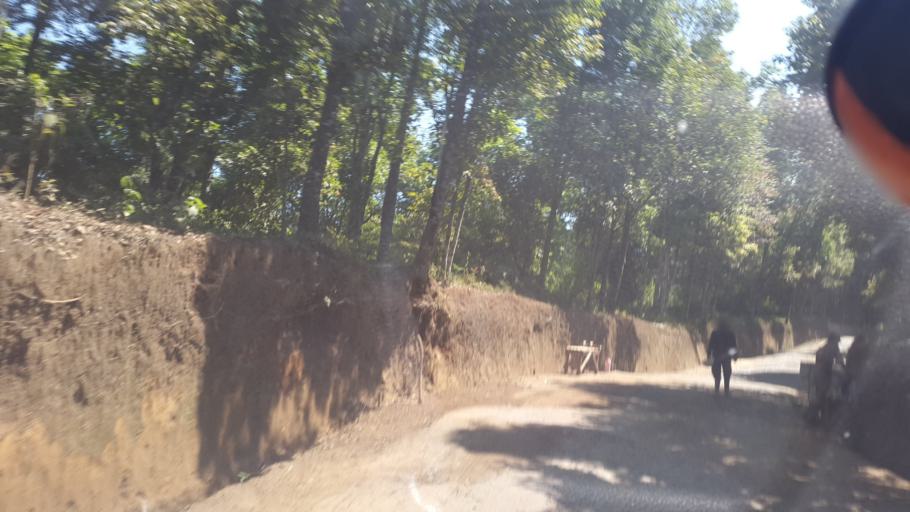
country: ID
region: Banten
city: Kubang
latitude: -6.7595
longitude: 106.6123
